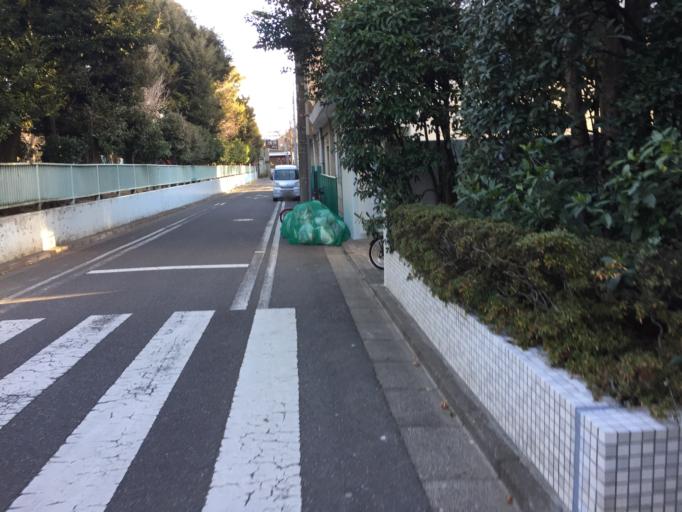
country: JP
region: Tokyo
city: Tokyo
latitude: 35.6421
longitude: 139.6786
